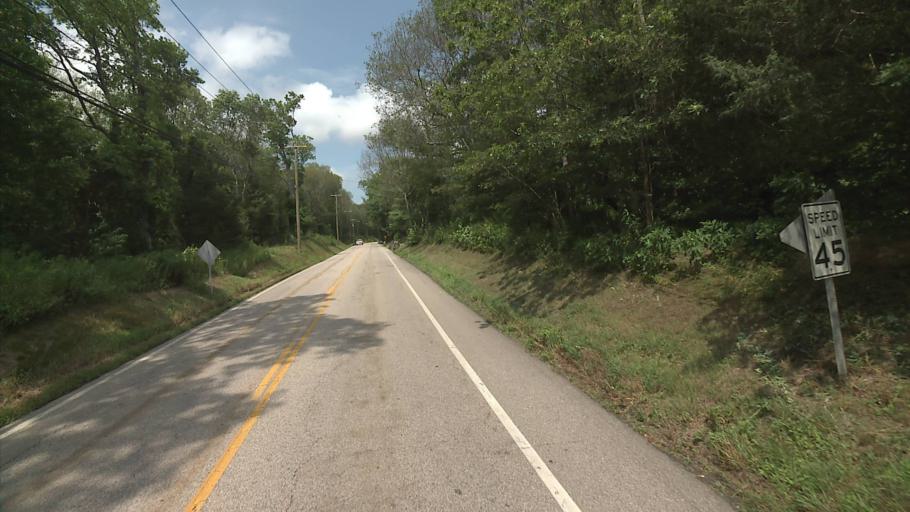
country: US
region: Connecticut
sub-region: New London County
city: Niantic
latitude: 41.4072
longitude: -72.2257
